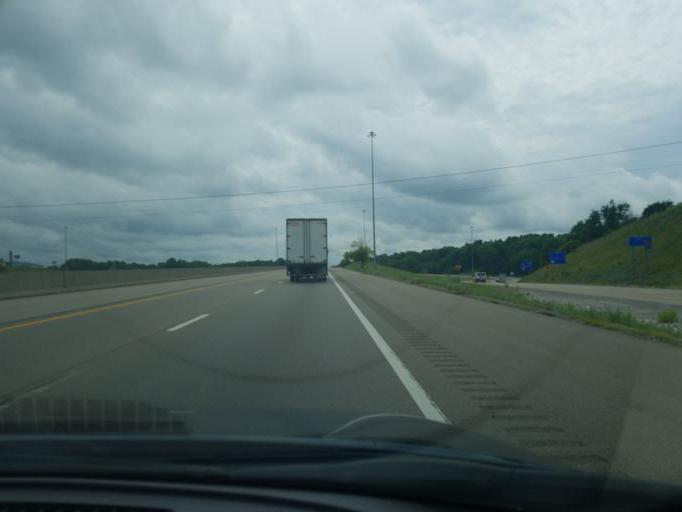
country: US
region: Kentucky
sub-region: Gallatin County
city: Warsaw
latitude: 38.7046
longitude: -84.9072
